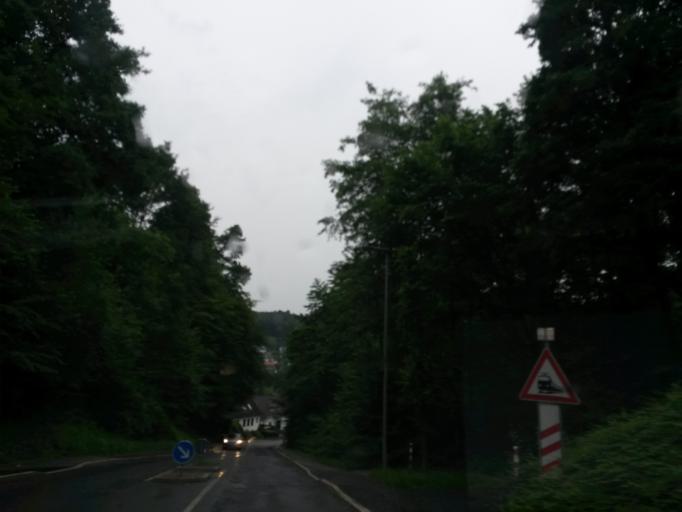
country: DE
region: North Rhine-Westphalia
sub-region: Regierungsbezirk Koln
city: Engelskirchen
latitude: 50.9719
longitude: 7.3660
